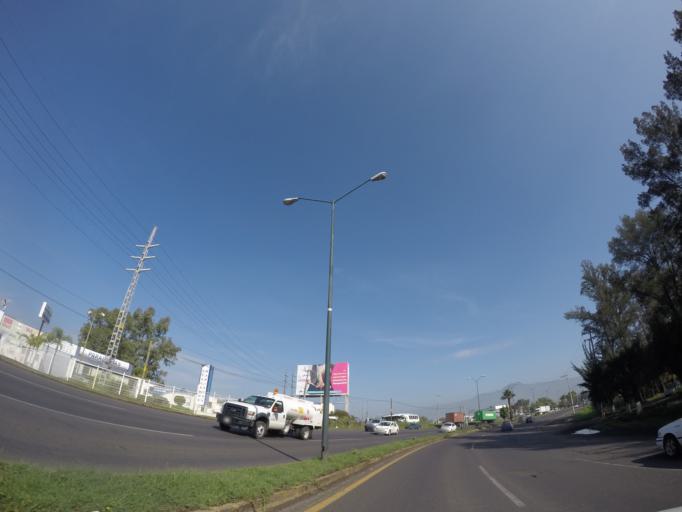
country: MX
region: Michoacan
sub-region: Morelia
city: Morelos
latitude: 19.6784
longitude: -101.2338
